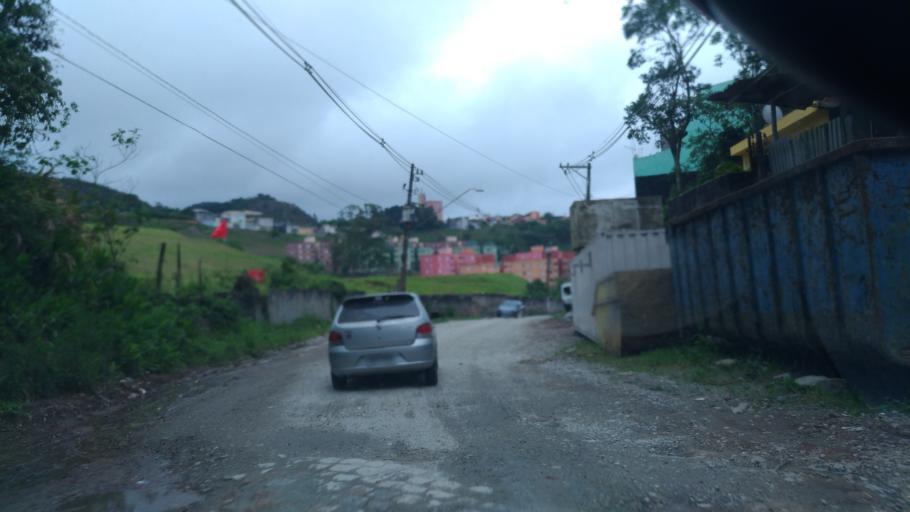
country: BR
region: Sao Paulo
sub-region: Sao Bernardo Do Campo
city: Sao Bernardo do Campo
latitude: -23.7405
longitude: -46.5208
